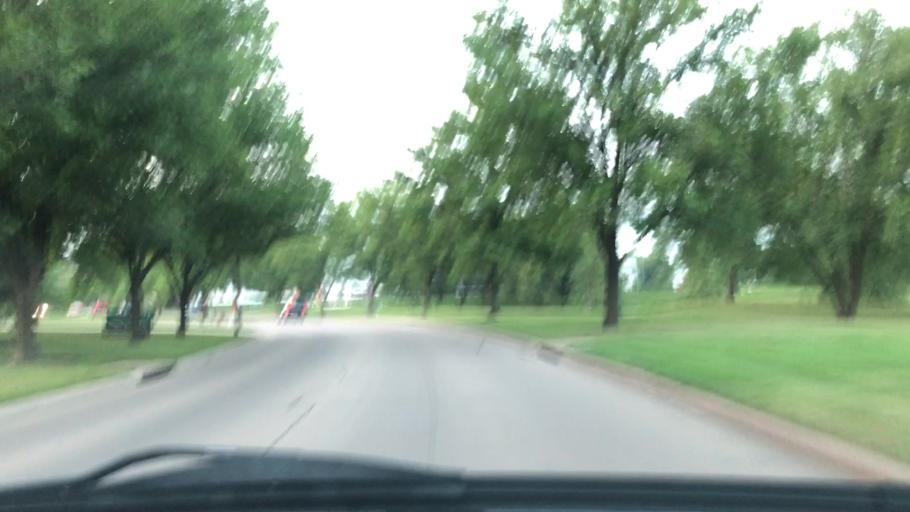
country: US
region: Iowa
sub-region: Johnson County
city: North Liberty
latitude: 41.7113
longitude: -91.6050
